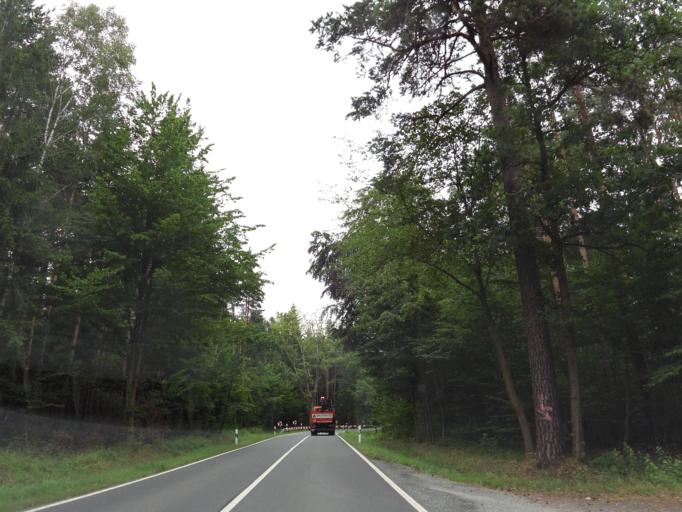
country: DE
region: Thuringia
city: Hainspitz
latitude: 50.9385
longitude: 11.8511
